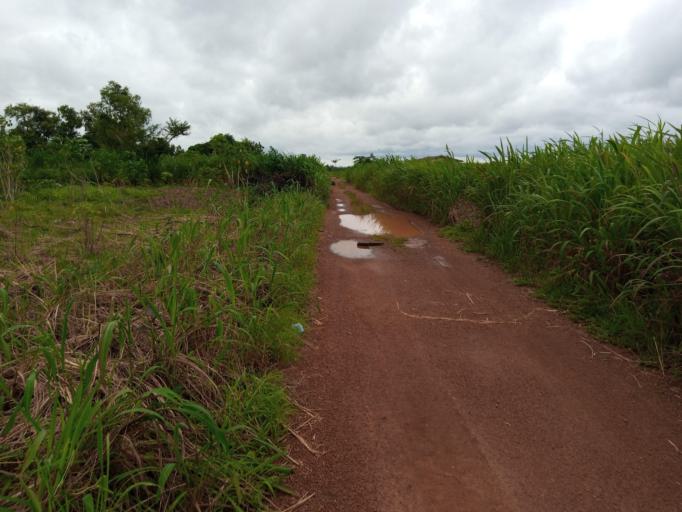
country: SL
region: Southern Province
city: Largo
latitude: 8.1968
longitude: -12.0477
